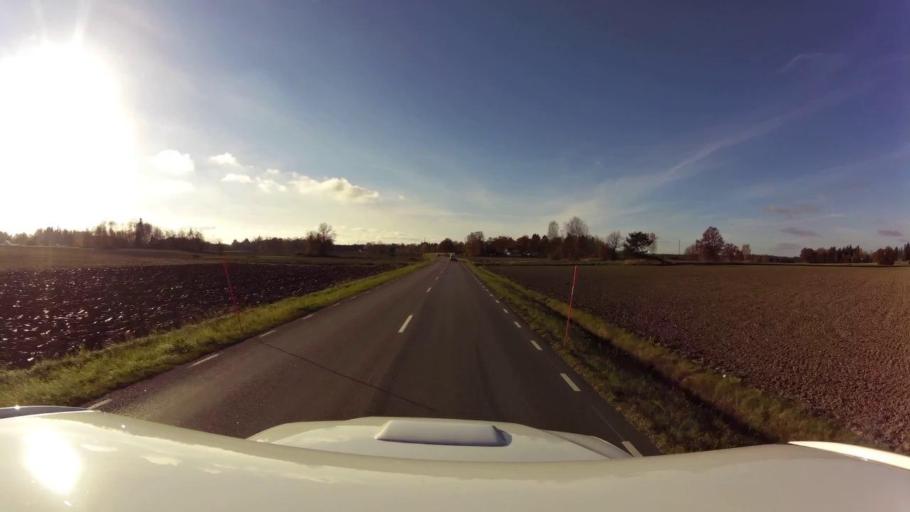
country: SE
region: OEstergoetland
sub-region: Linkopings Kommun
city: Malmslatt
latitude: 58.3479
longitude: 15.5367
